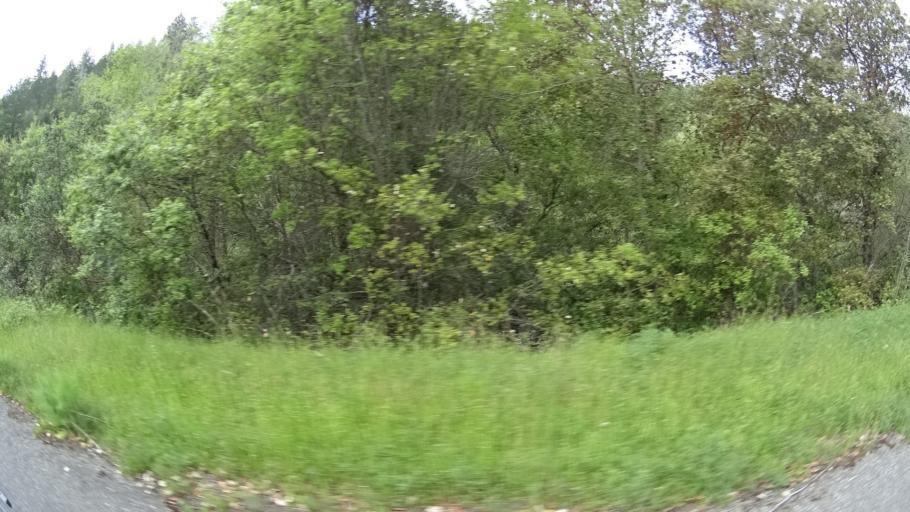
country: US
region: California
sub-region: Humboldt County
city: Redway
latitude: 40.1924
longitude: -123.5899
